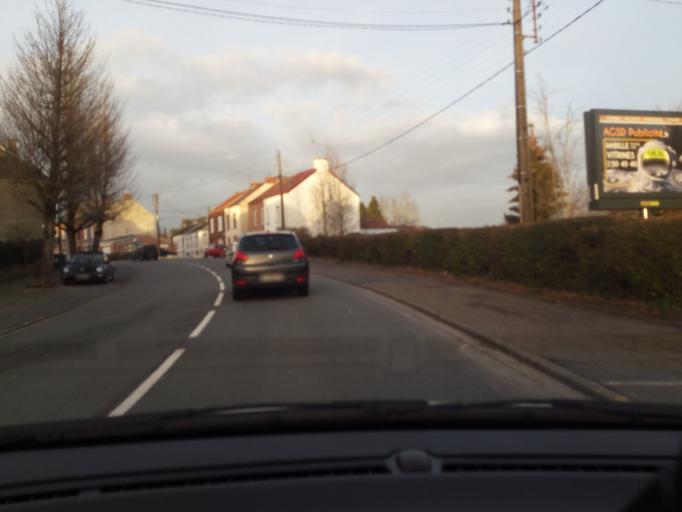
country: FR
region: Nord-Pas-de-Calais
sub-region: Departement du Nord
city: Louvroil
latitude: 50.2612
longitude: 3.9614
